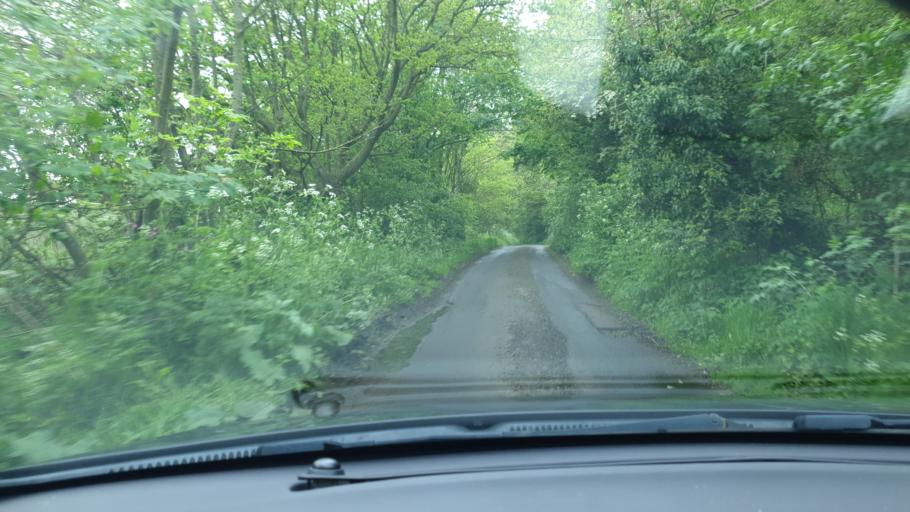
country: GB
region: England
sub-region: Essex
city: Dovercourt
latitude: 51.9118
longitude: 1.1991
